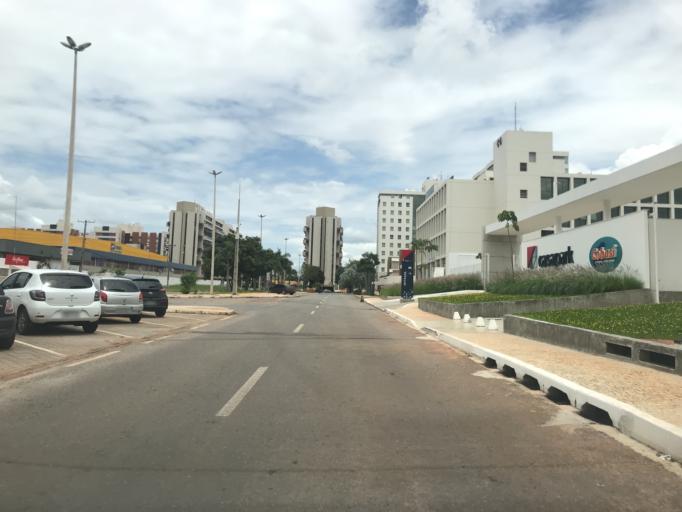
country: BR
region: Federal District
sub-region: Brasilia
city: Brasilia
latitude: -15.8266
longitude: -47.9547
